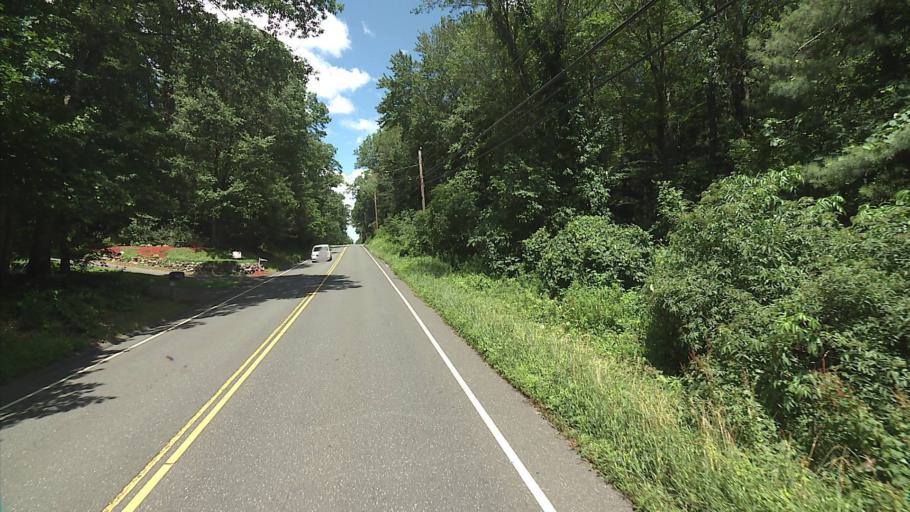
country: US
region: Connecticut
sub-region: Litchfield County
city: New Hartford Center
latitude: 41.9307
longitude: -72.9203
